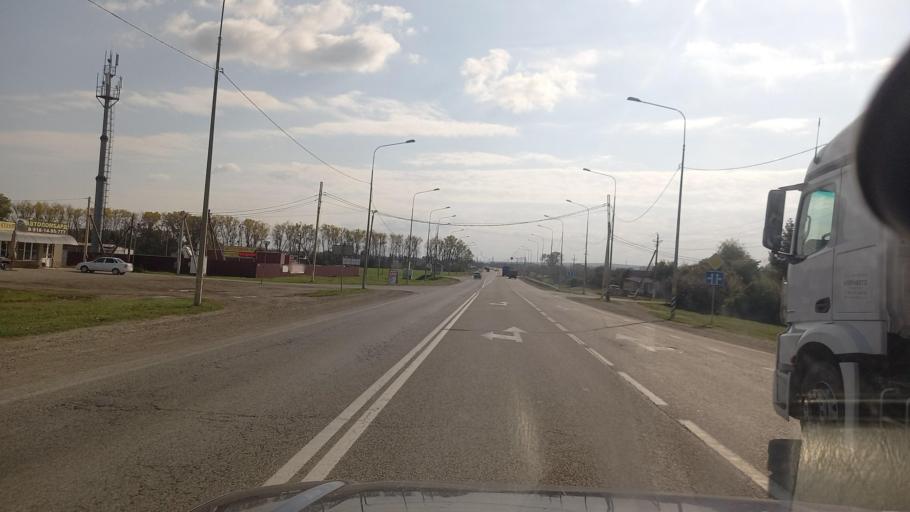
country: RU
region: Krasnodarskiy
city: Novoukrainskiy
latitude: 44.9037
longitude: 38.0322
